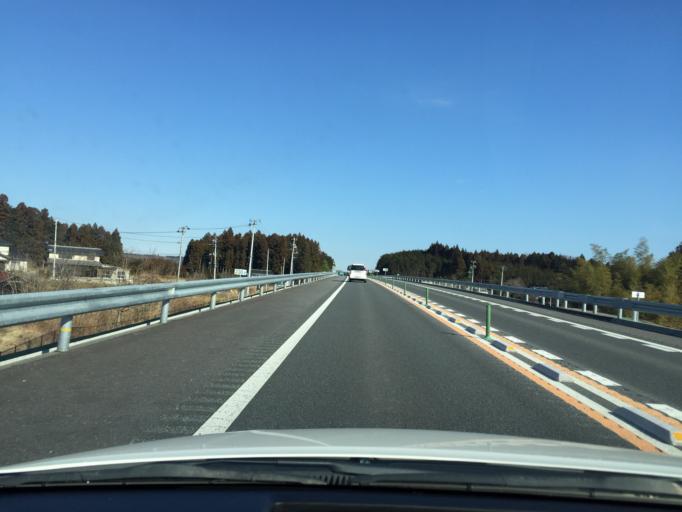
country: JP
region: Fukushima
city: Namie
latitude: 37.5481
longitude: 140.9435
